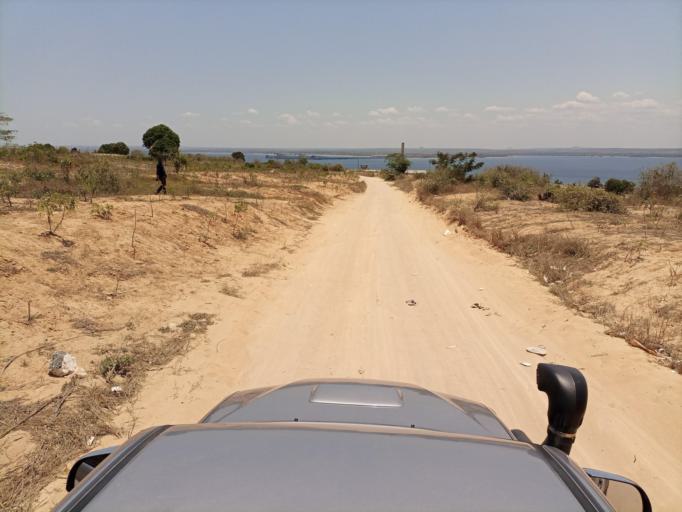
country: MZ
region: Nampula
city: Nacala
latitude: -14.5174
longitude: 40.6832
